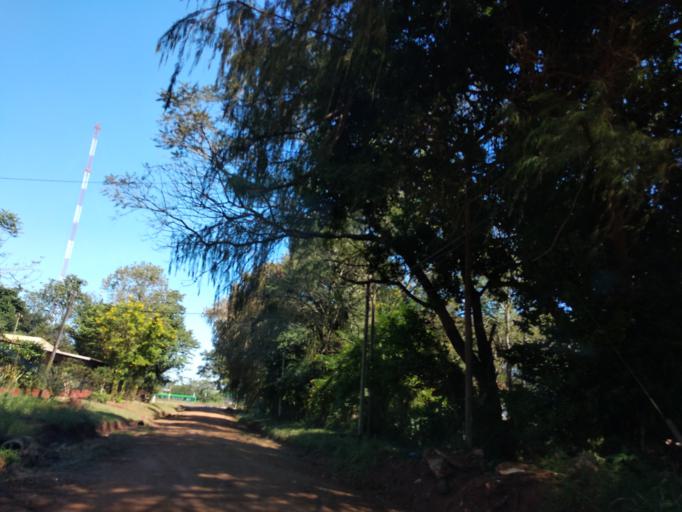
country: AR
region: Misiones
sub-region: Departamento de Capital
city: Posadas
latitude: -27.4296
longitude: -55.8890
